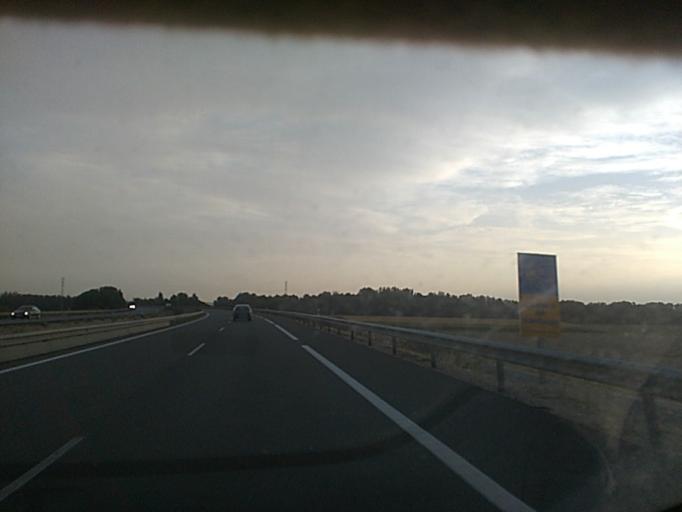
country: ES
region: Castille and Leon
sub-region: Provincia de Valladolid
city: Tordesillas
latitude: 41.4848
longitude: -4.9871
